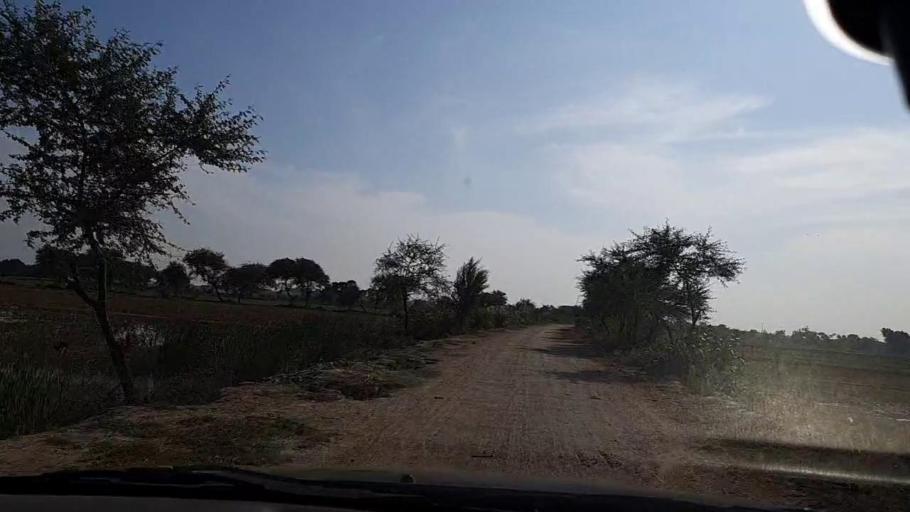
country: PK
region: Sindh
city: Mirpur Batoro
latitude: 24.6171
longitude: 68.2702
